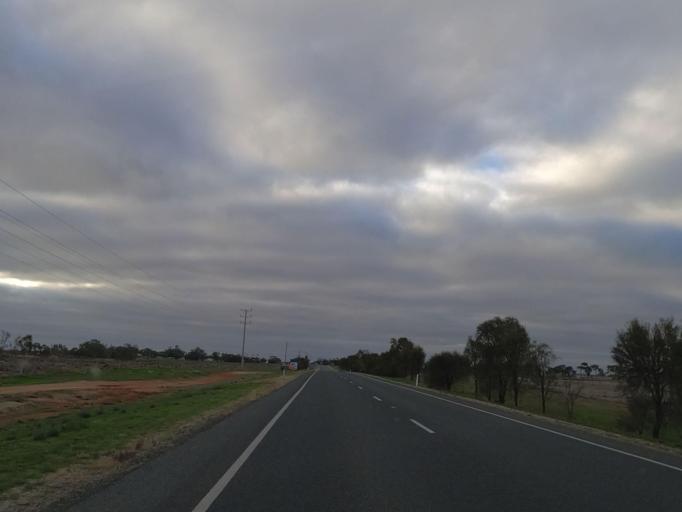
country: AU
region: Victoria
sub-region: Swan Hill
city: Swan Hill
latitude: -35.6178
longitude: 143.8034
